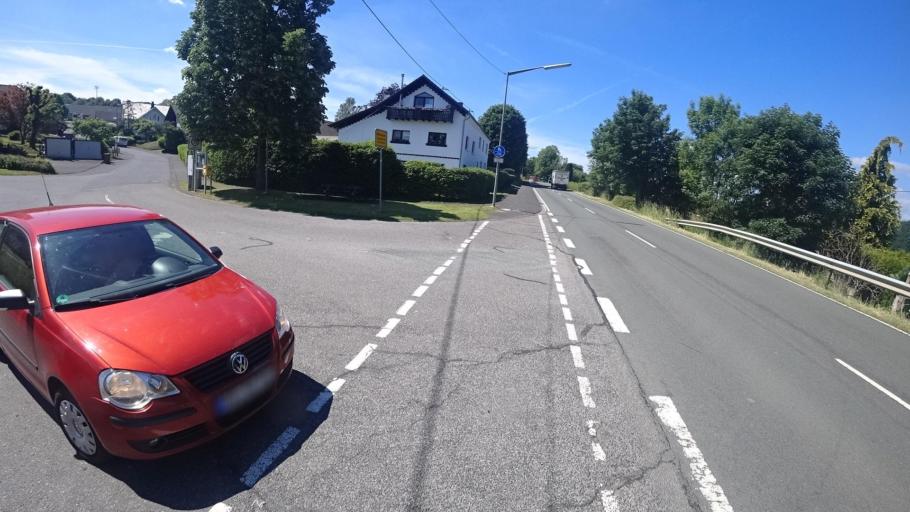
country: DE
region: Rheinland-Pfalz
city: Mammelzen
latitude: 50.6984
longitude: 7.6589
